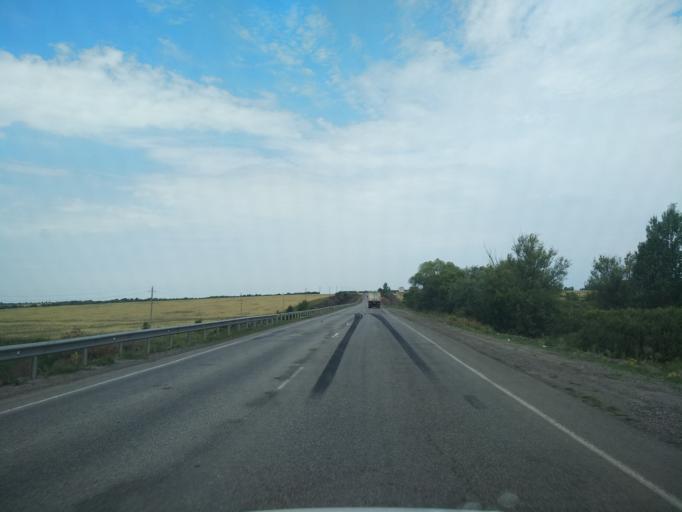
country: RU
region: Voronezj
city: Verkhnyaya Khava
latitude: 51.6753
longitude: 39.8159
